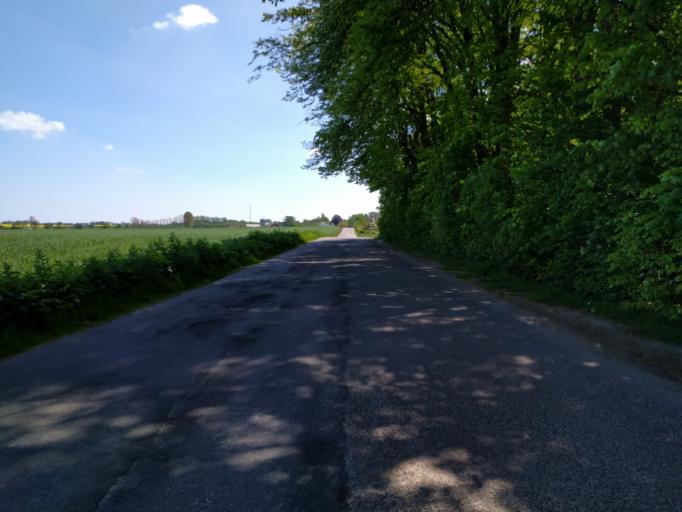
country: DK
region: Zealand
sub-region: Guldborgsund Kommune
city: Nykobing Falster
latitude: 54.7466
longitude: 11.9463
